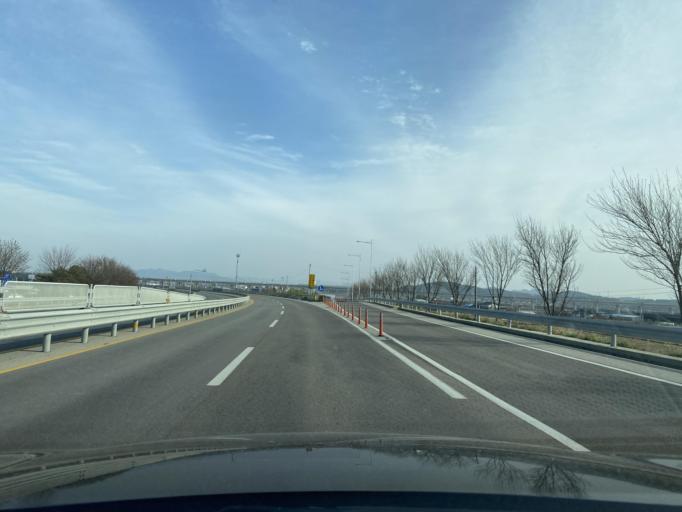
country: KR
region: Chungcheongnam-do
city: Hongsung
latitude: 36.6885
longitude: 126.7145
